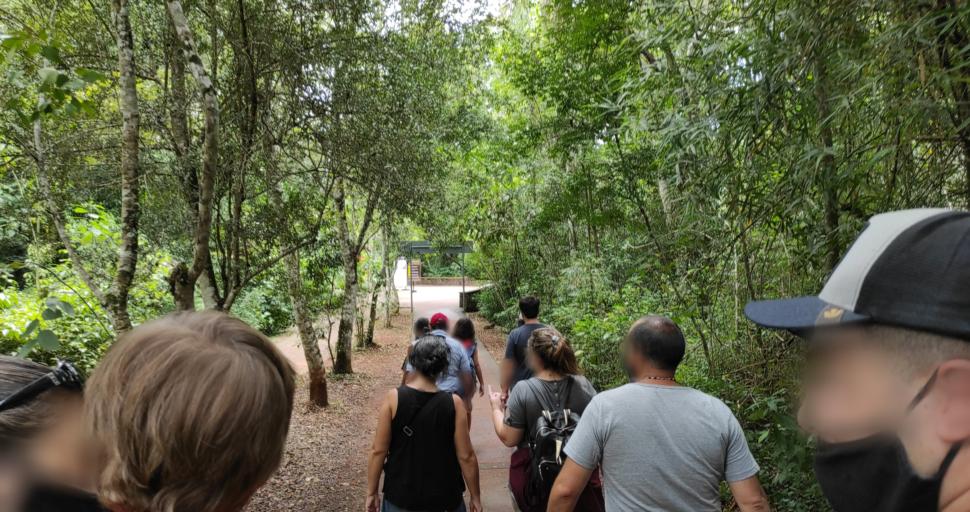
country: AR
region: Misiones
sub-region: Departamento de Iguazu
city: Puerto Iguazu
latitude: -25.6841
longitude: -54.4471
